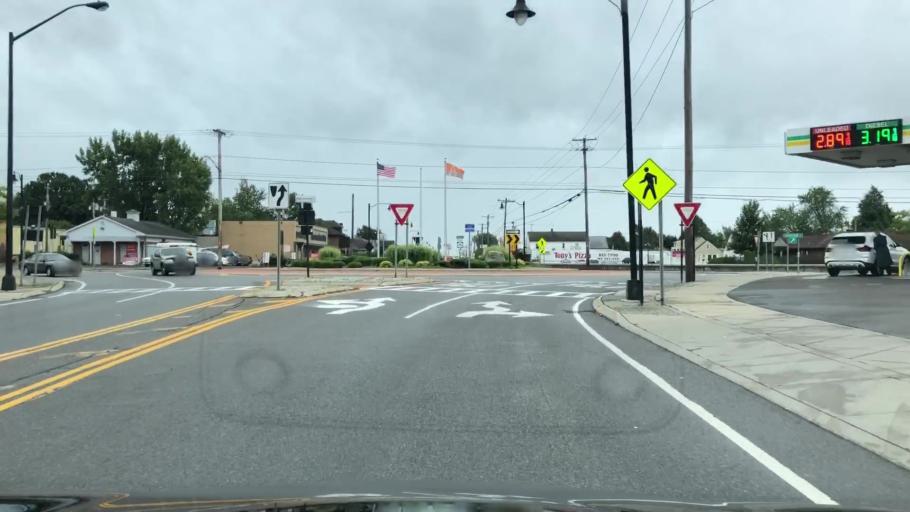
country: US
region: New York
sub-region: Erie County
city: Eggertsville
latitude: 42.9455
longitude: -78.7842
